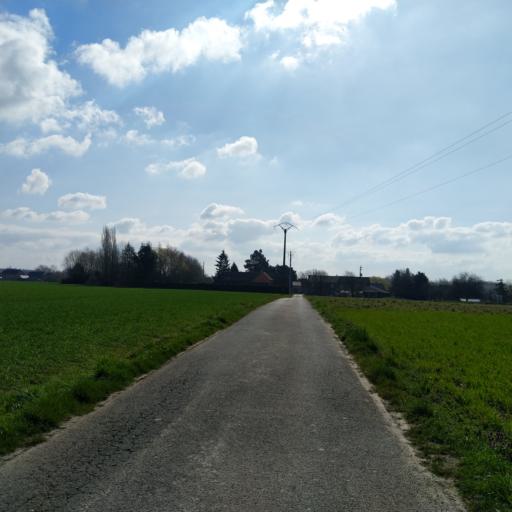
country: BE
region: Wallonia
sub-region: Province du Hainaut
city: Lens
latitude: 50.5798
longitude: 3.9169
